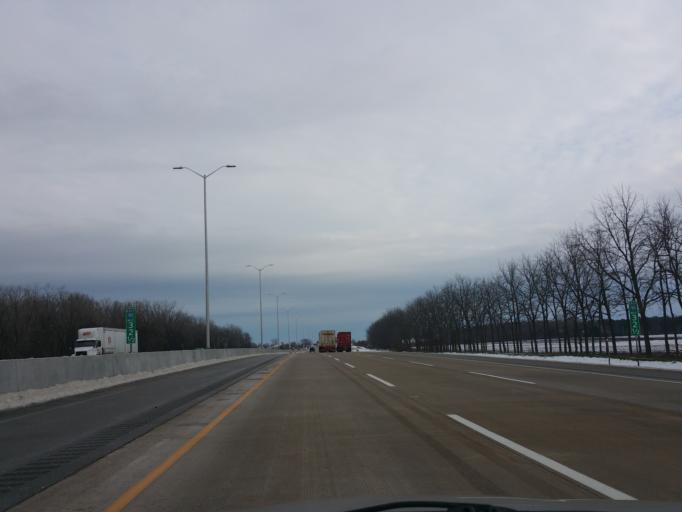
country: US
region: Illinois
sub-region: McHenry County
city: Marengo
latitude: 42.1998
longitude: -88.6826
